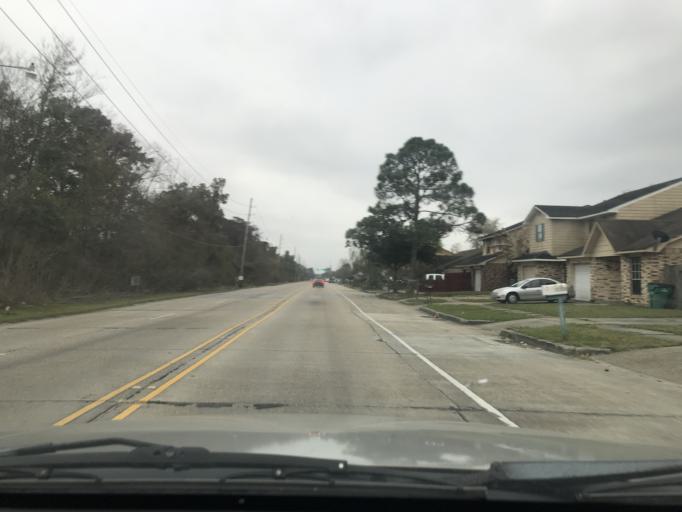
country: US
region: Louisiana
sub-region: Jefferson Parish
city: Woodmere
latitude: 29.8606
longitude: -90.0725
